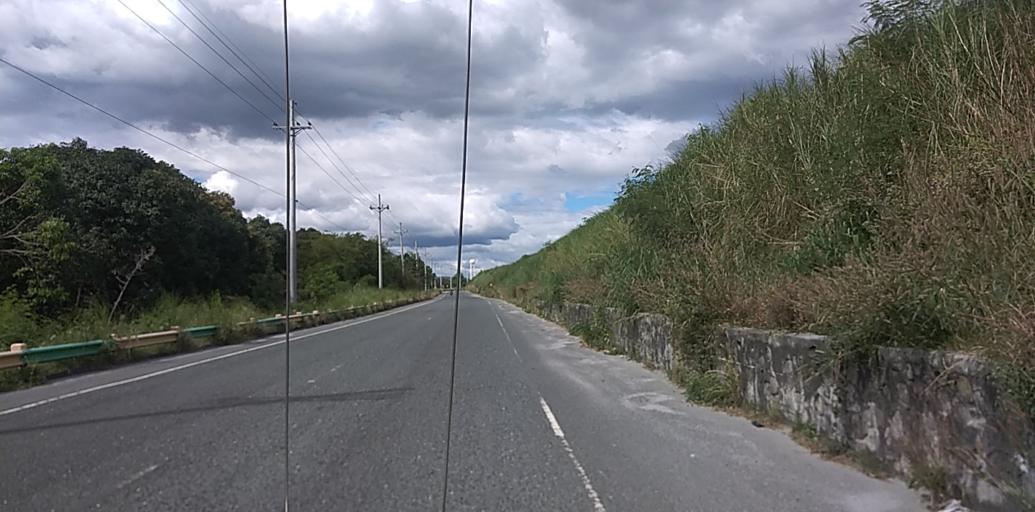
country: PH
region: Central Luzon
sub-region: Province of Pampanga
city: Dolores
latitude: 15.1031
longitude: 120.5226
